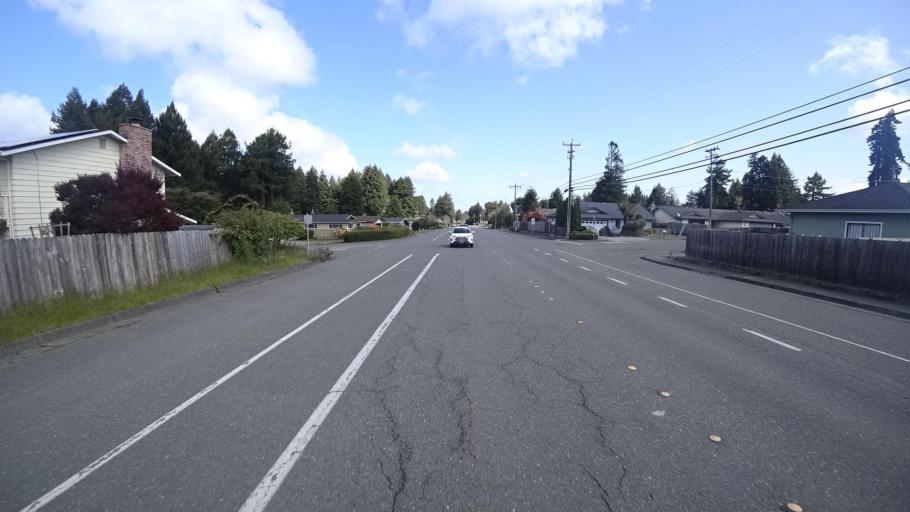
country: US
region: California
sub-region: Humboldt County
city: Pine Hills
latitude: 40.7404
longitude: -124.1475
